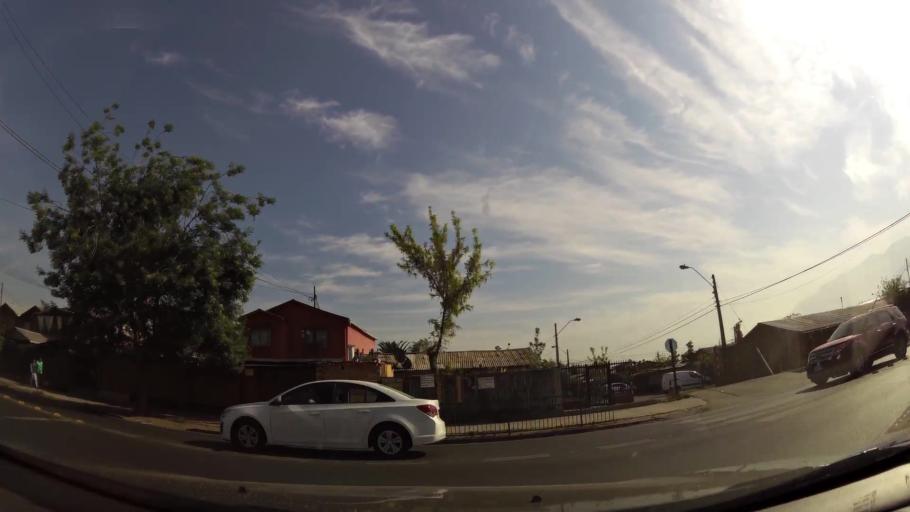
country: CL
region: Santiago Metropolitan
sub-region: Provincia de Cordillera
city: Puente Alto
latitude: -33.5617
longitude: -70.5724
